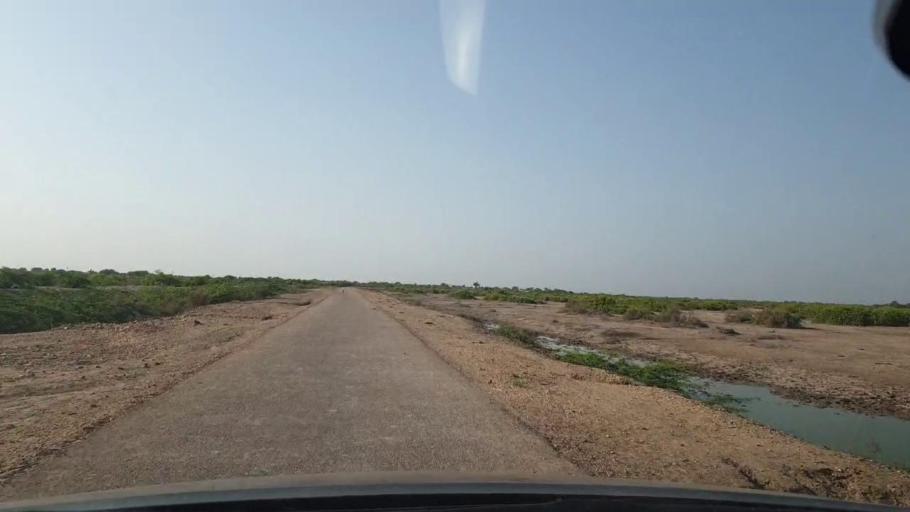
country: PK
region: Sindh
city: Naukot
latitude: 24.8282
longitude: 69.2265
